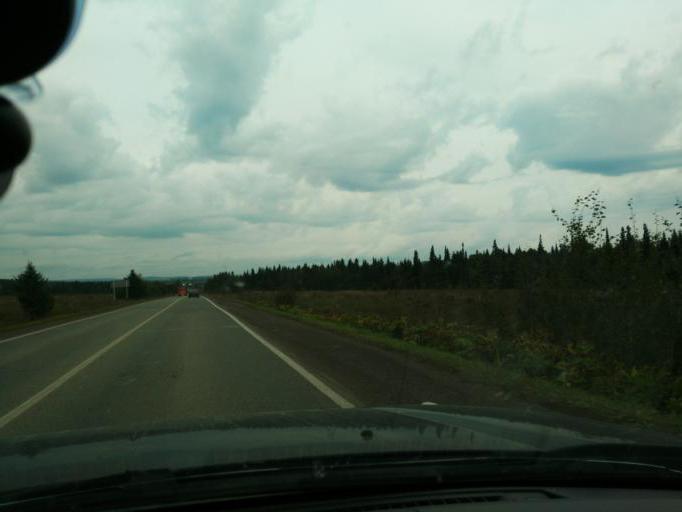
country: RU
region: Perm
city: Chernushka
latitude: 56.7151
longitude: 56.1811
